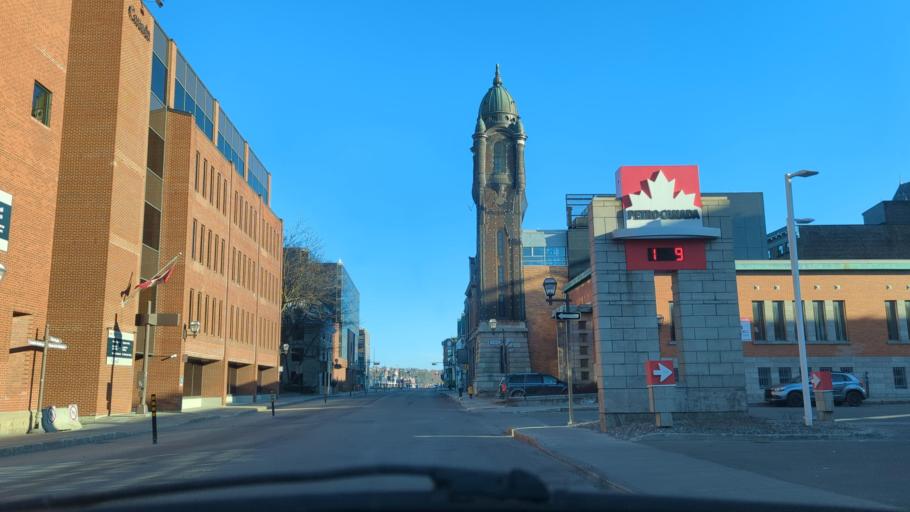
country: CA
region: Quebec
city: Quebec
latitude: 46.8167
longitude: -71.2024
